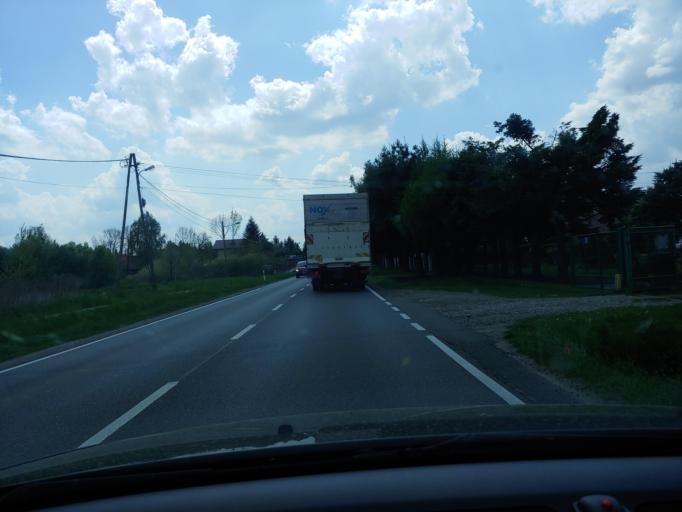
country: PL
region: Lesser Poland Voivodeship
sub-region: Powiat tarnowski
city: Lisia Gora
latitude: 50.0620
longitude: 21.0136
